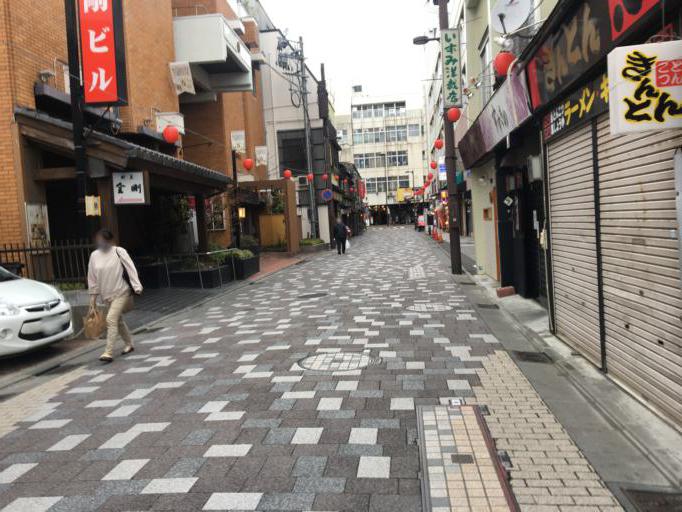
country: JP
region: Aomori
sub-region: Hachinohe Shi
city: Uchimaru
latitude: 40.5084
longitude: 141.4920
